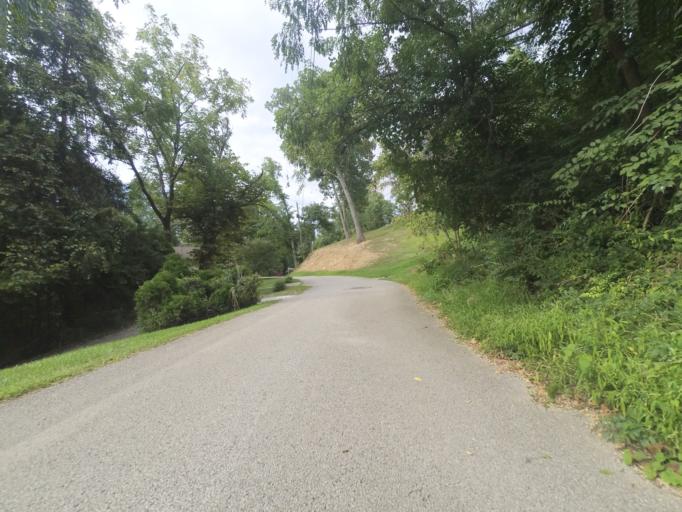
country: US
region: West Virginia
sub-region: Cabell County
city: Huntington
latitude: 38.4021
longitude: -82.4464
